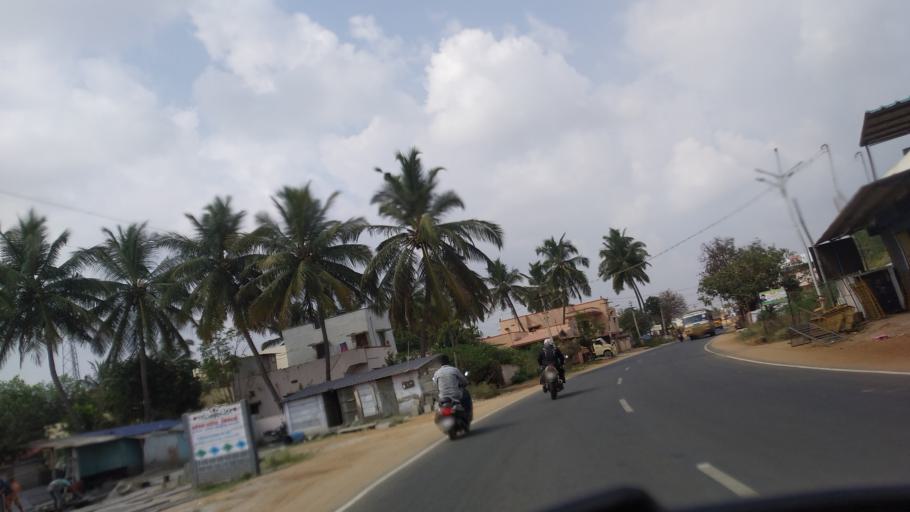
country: IN
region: Tamil Nadu
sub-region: Coimbatore
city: Perur
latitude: 10.9547
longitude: 76.9284
